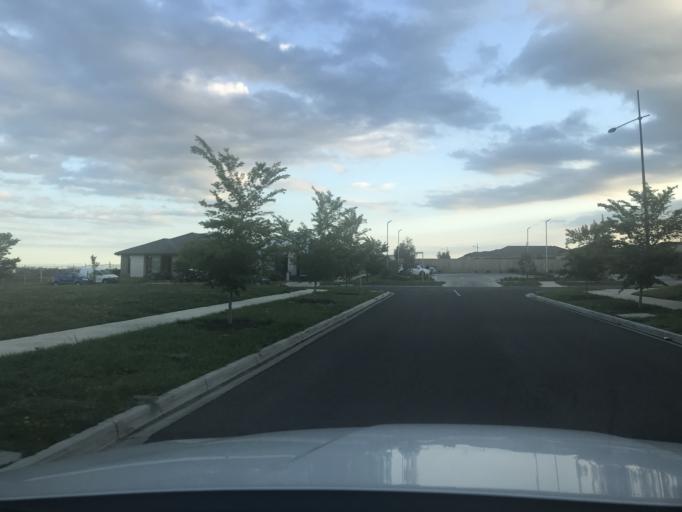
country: AU
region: Victoria
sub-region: Hume
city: Roxburgh Park
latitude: -37.5726
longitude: 144.8929
